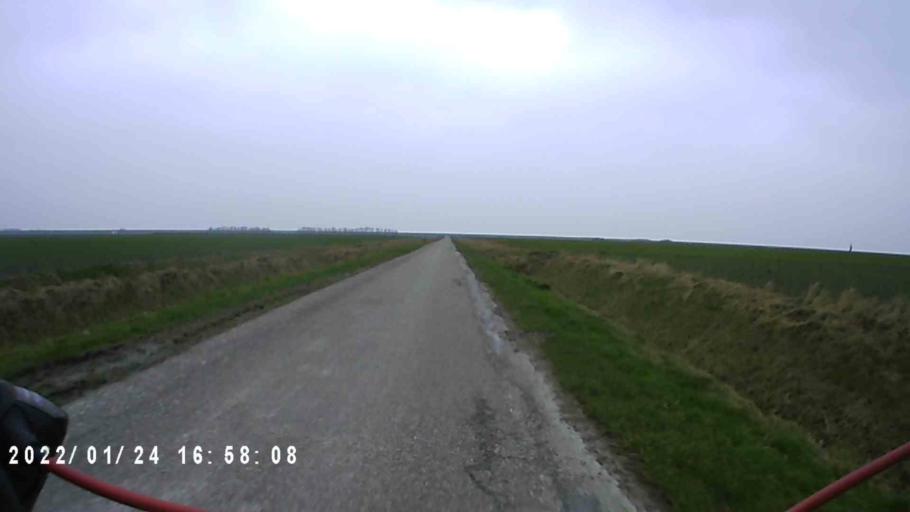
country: NL
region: Groningen
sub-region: Gemeente De Marne
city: Ulrum
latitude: 53.3889
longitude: 6.3347
